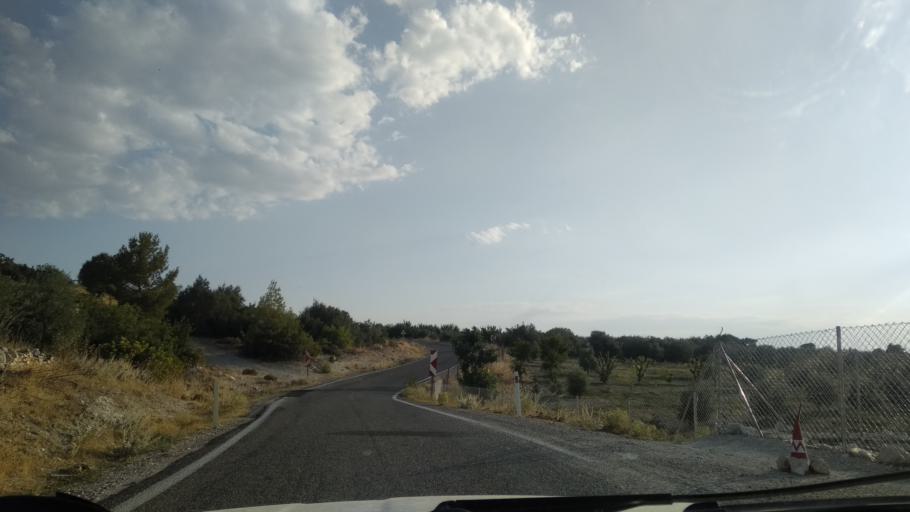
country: TR
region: Mersin
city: Sarikavak
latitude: 36.5696
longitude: 33.6344
